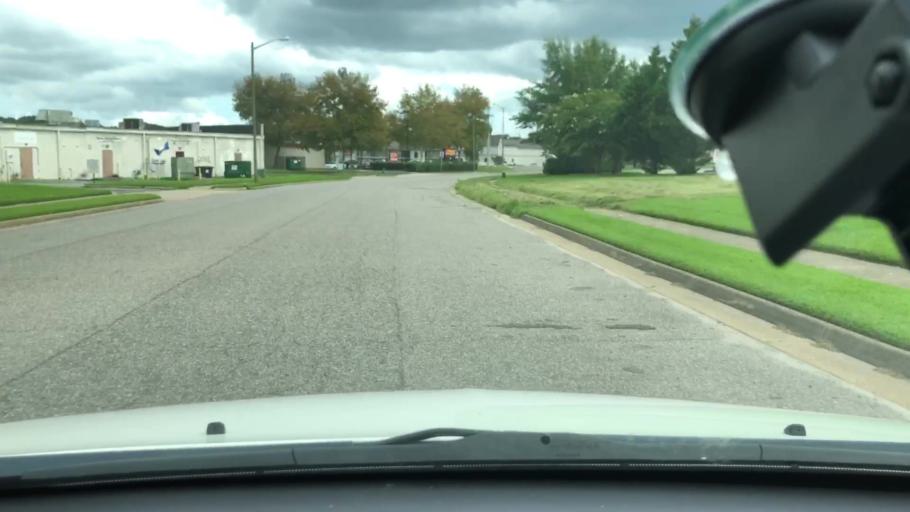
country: US
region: Virginia
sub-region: City of Chesapeake
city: Chesapeake
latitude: 36.7780
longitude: -76.2710
